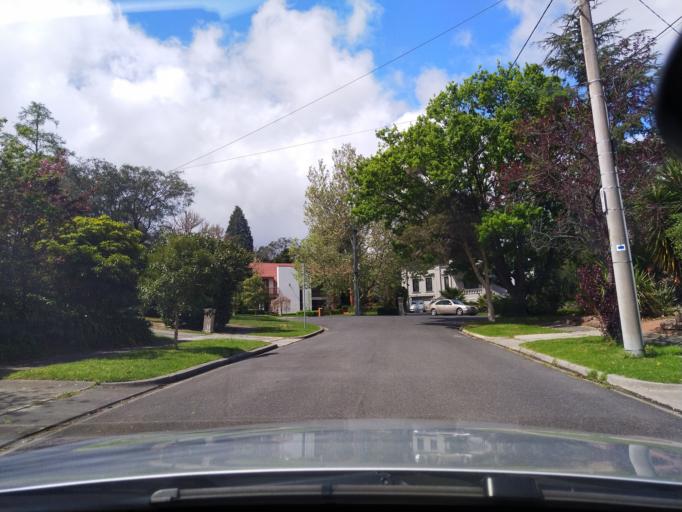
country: AU
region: Victoria
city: Rosanna
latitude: -37.7629
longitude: 145.0576
